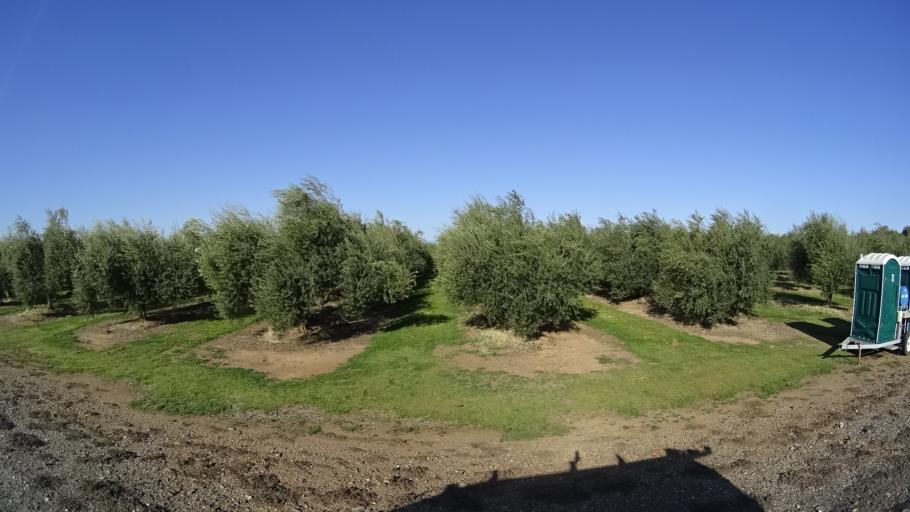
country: US
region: California
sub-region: Glenn County
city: Orland
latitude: 39.7622
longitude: -122.1134
